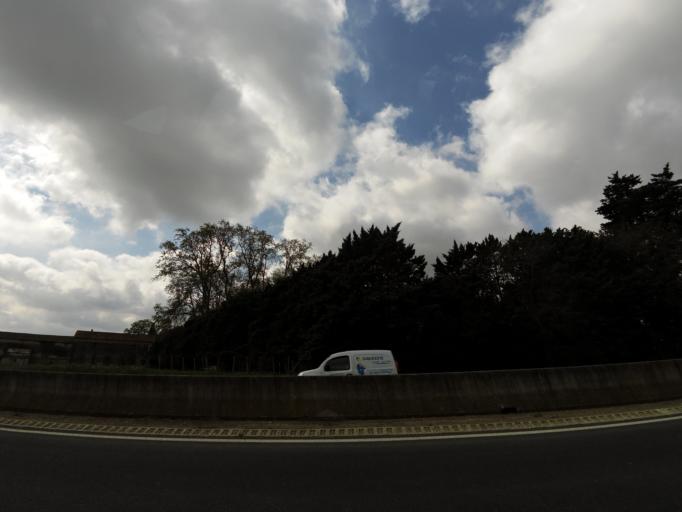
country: FR
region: Languedoc-Roussillon
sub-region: Departement du Gard
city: Aimargues
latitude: 43.6910
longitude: 4.2090
